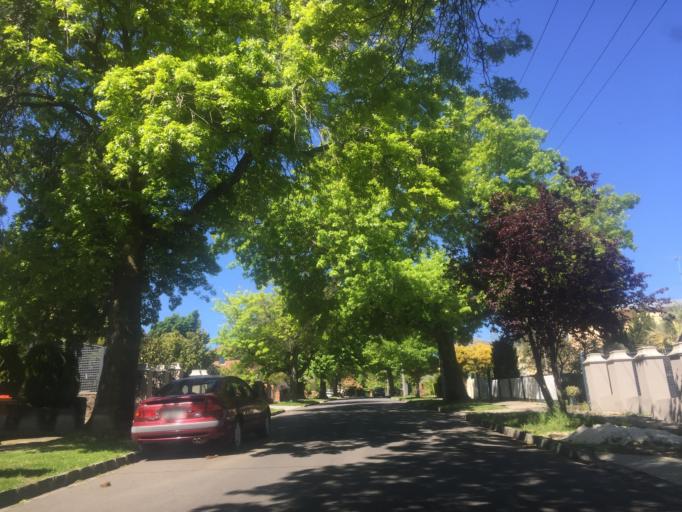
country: AU
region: Victoria
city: Balwyn
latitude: -37.8060
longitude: 145.0812
